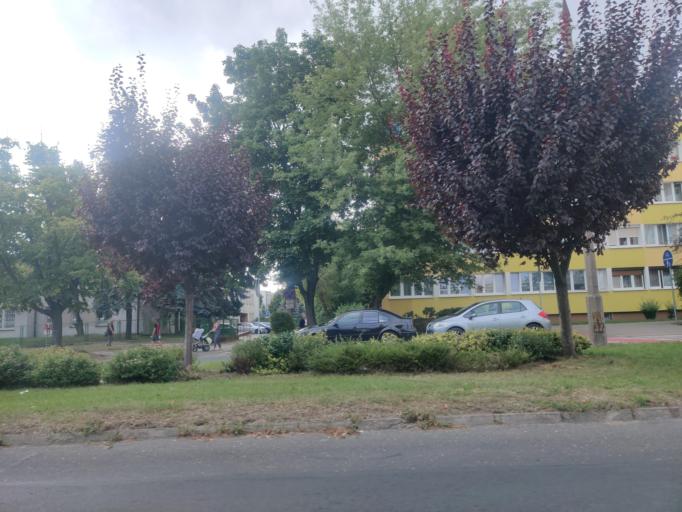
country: PL
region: Greater Poland Voivodeship
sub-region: Konin
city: Konin
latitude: 52.2291
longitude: 18.2722
